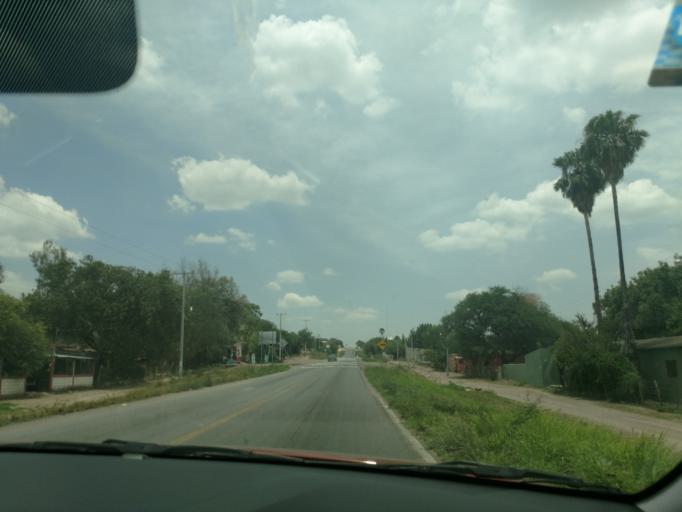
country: MX
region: San Luis Potosi
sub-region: Rioverde
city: Progreso
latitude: 22.0193
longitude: -100.3773
